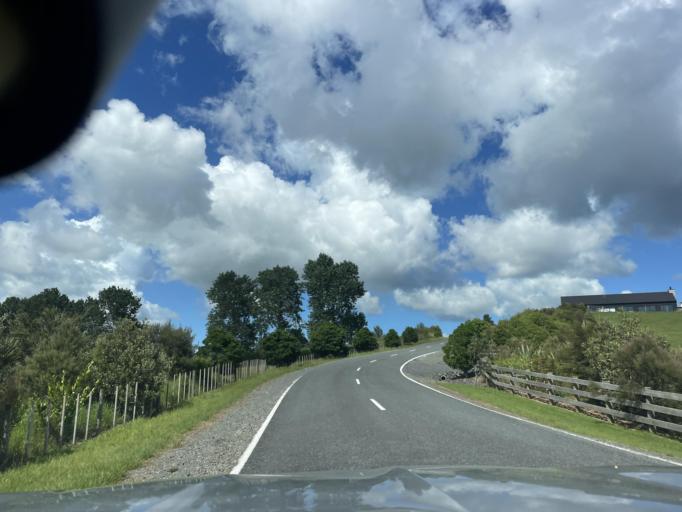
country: NZ
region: Northland
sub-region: Whangarei
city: Ruakaka
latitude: -36.0852
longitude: 174.5332
